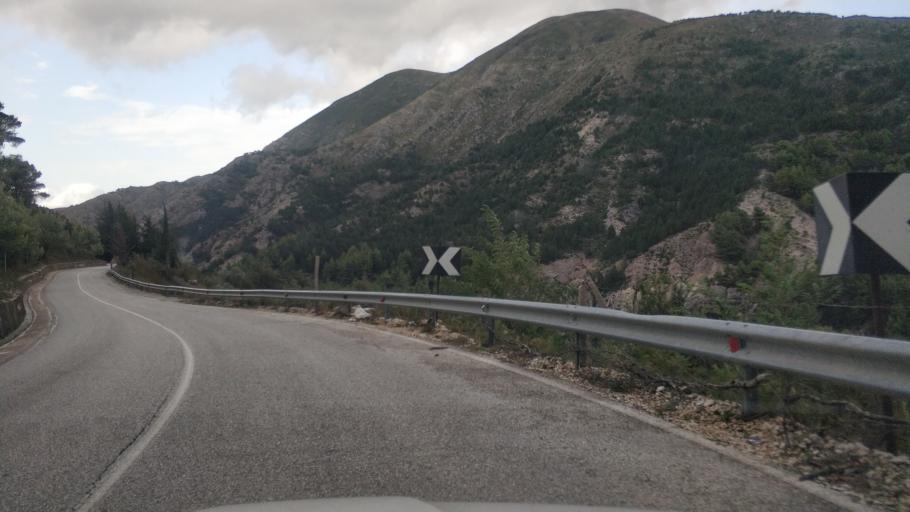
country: AL
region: Vlore
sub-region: Rrethi i Vlores
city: Orikum
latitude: 40.2443
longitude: 19.5507
